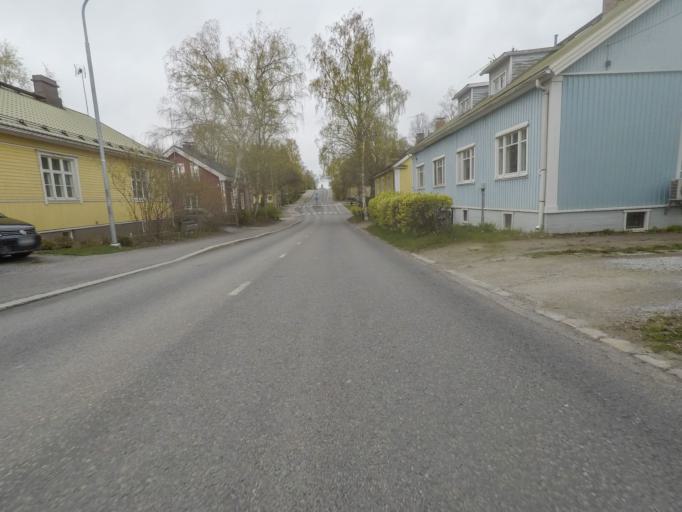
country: FI
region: Pirkanmaa
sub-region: Tampere
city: Tampere
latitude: 61.4841
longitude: 23.7878
